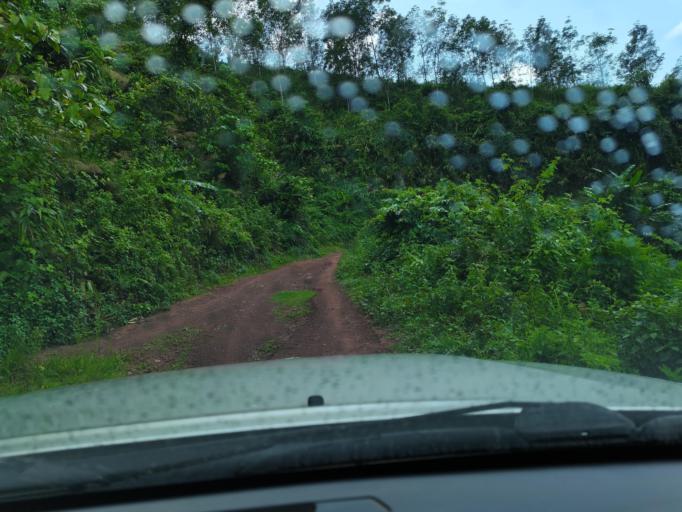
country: LA
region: Loungnamtha
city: Muang Nale
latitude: 20.5251
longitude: 101.0674
